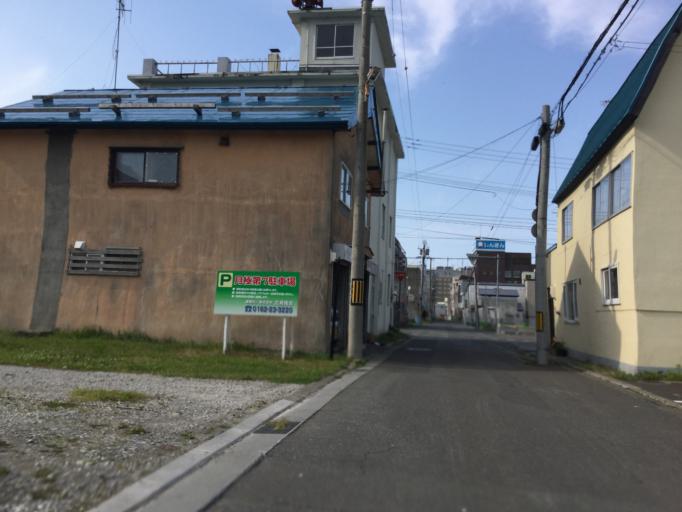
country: JP
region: Hokkaido
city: Wakkanai
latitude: 45.4144
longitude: 141.6746
